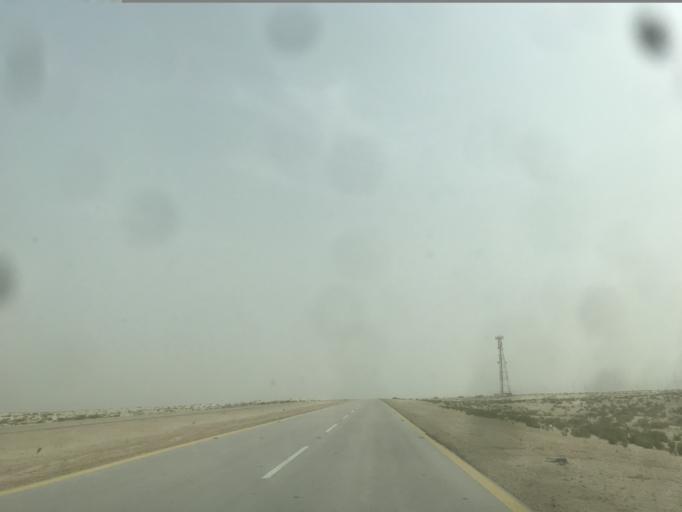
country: SA
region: Eastern Province
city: Abqaiq
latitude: 25.9096
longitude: 49.9709
